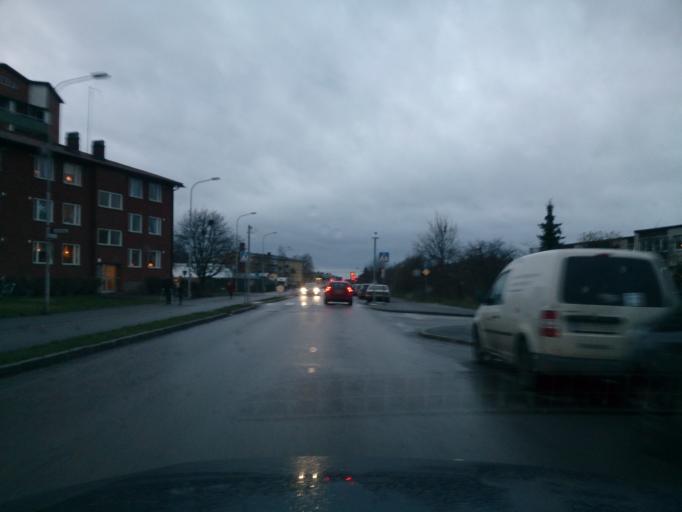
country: SE
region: OEstergoetland
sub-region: Norrkopings Kommun
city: Norrkoping
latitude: 58.6084
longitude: 16.1451
